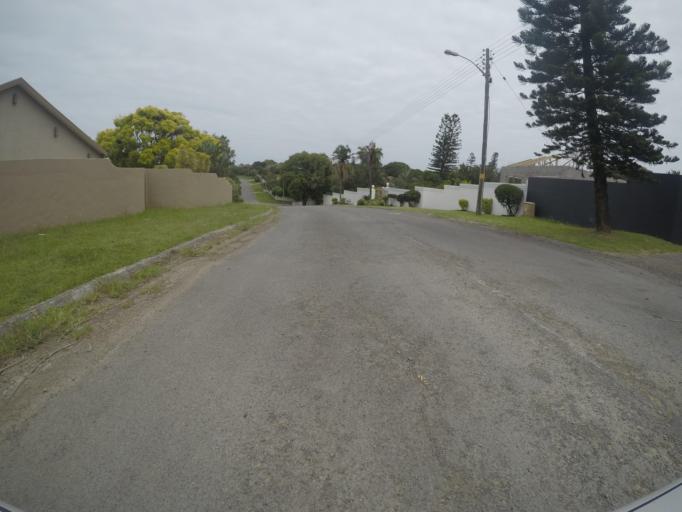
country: ZA
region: Eastern Cape
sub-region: Buffalo City Metropolitan Municipality
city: East London
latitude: -32.9731
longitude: 27.9438
